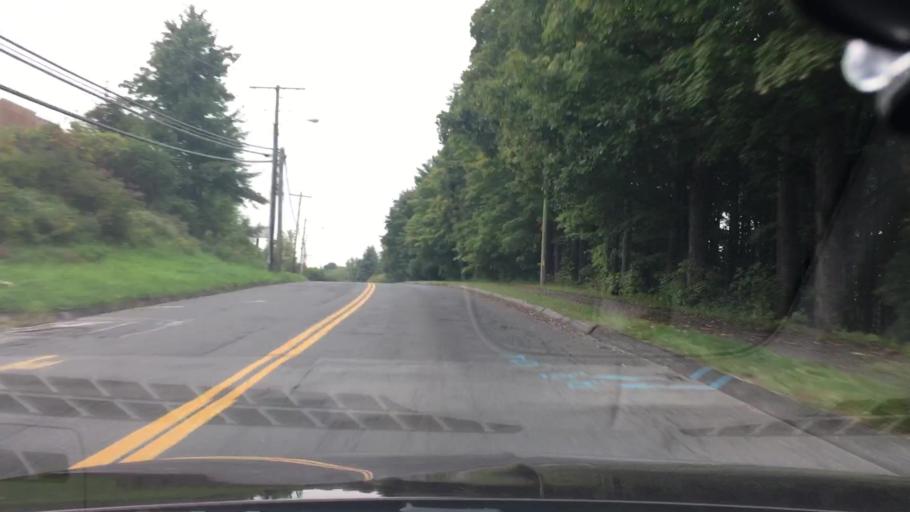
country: US
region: Connecticut
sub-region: Hartford County
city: Kensington
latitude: 41.5874
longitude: -72.7203
